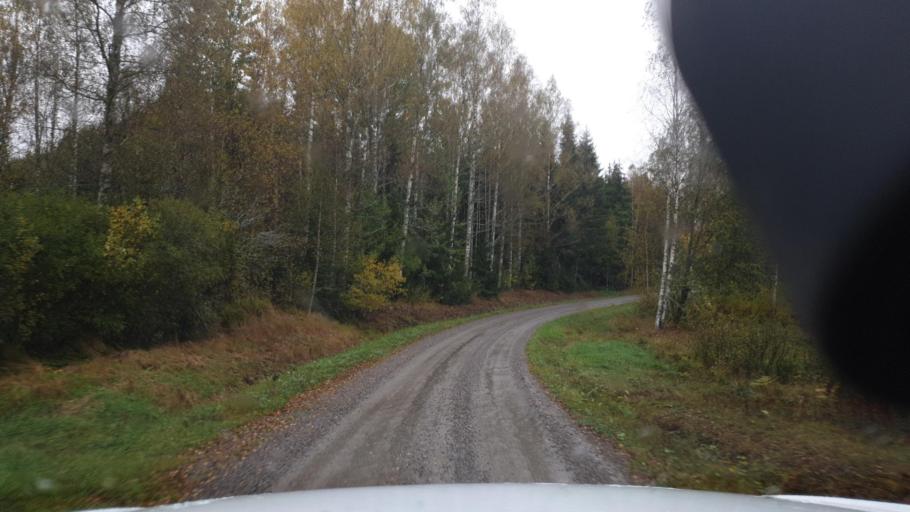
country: SE
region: Vaermland
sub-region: Arvika Kommun
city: Arvika
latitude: 59.5539
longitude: 12.8471
